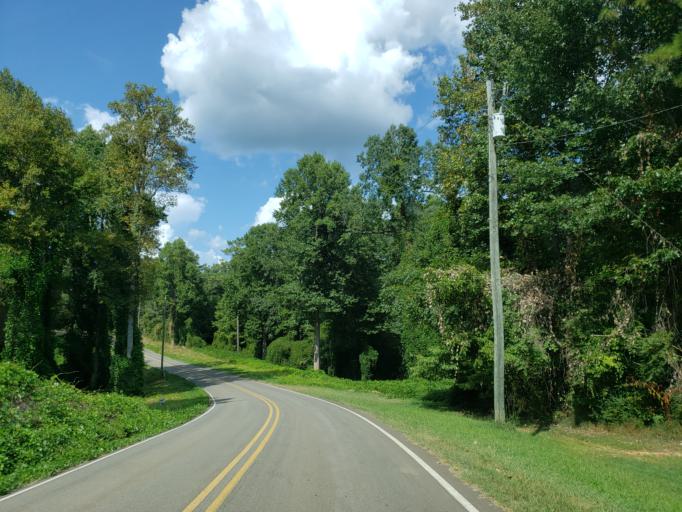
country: US
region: Georgia
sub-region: Pickens County
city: Jasper
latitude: 34.4237
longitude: -84.4403
